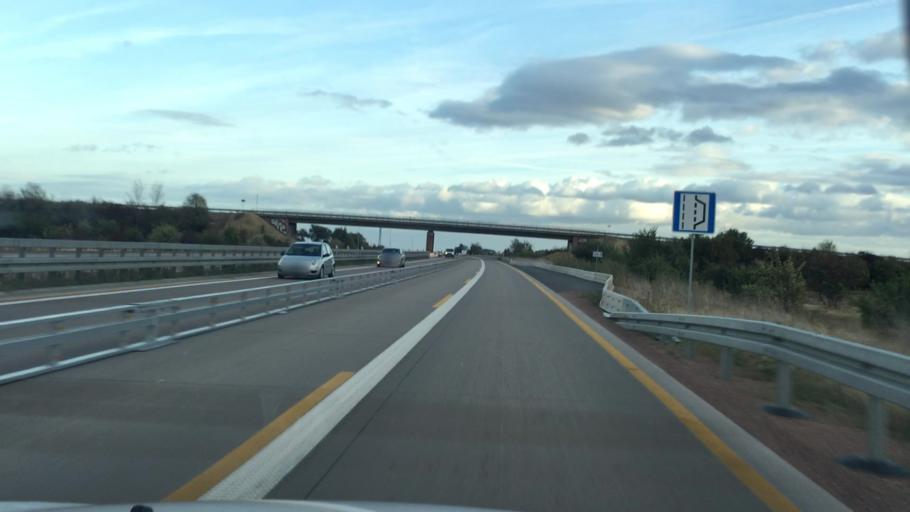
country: DE
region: Saxony-Anhalt
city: Nauendorf
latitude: 51.5853
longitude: 11.8802
